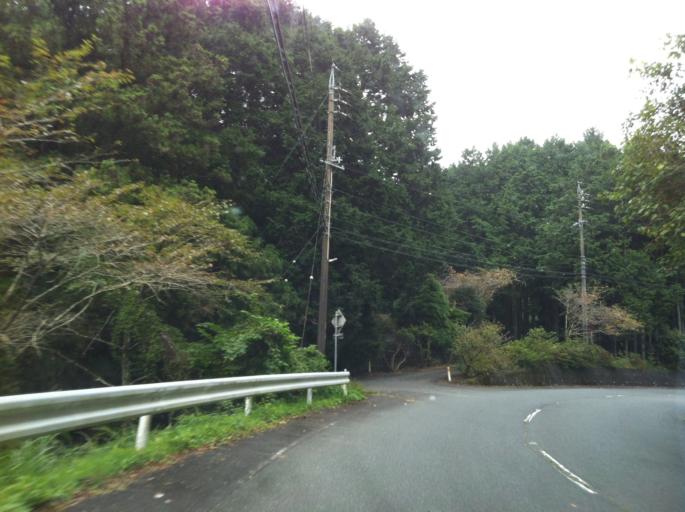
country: JP
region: Shizuoka
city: Mori
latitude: 34.8709
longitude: 138.0186
